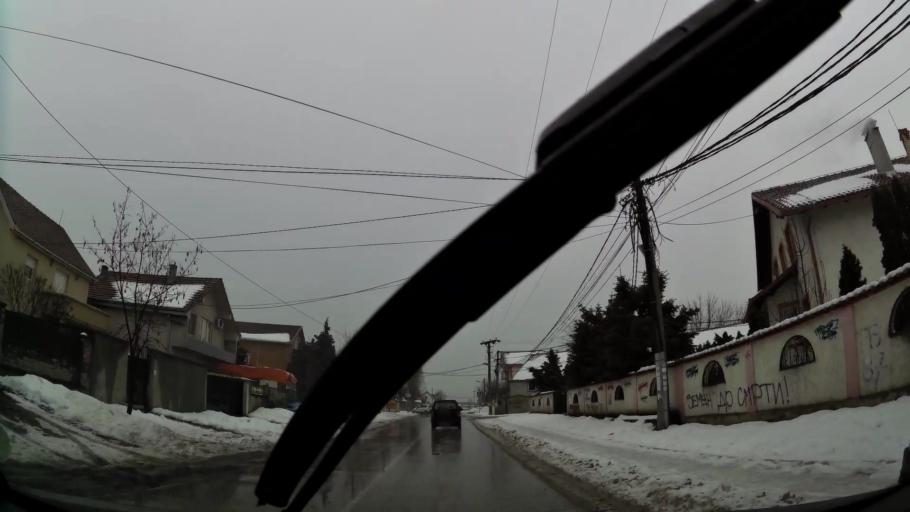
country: RS
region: Central Serbia
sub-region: Belgrade
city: Zemun
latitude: 44.8484
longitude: 20.3546
